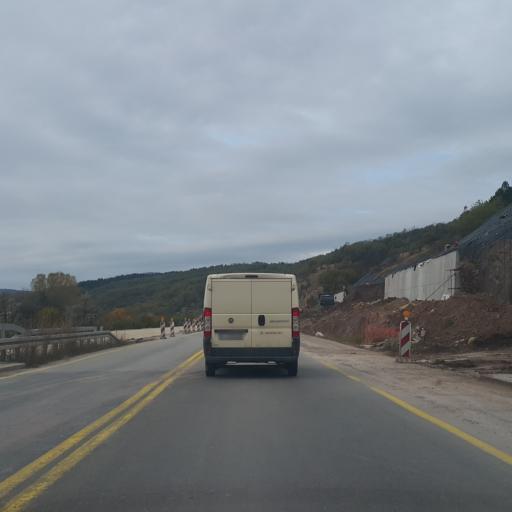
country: RS
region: Central Serbia
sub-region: Pirotski Okrug
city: Pirot
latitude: 43.2291
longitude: 22.4628
